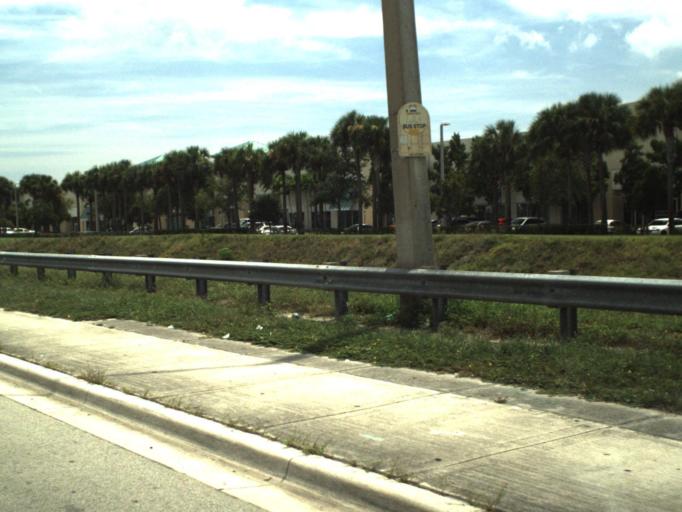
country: US
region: Florida
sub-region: Broward County
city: Pompano Beach
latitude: 26.2313
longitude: -80.1506
